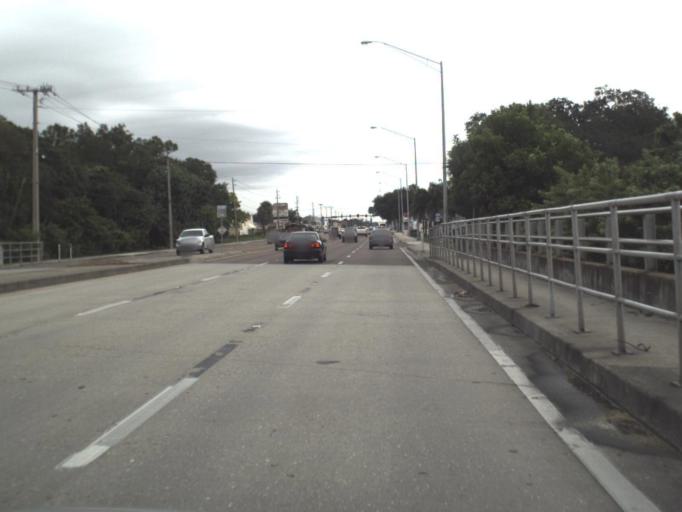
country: US
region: Florida
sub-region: Sarasota County
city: Ridge Wood Heights
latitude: 27.2988
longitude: -82.5189
